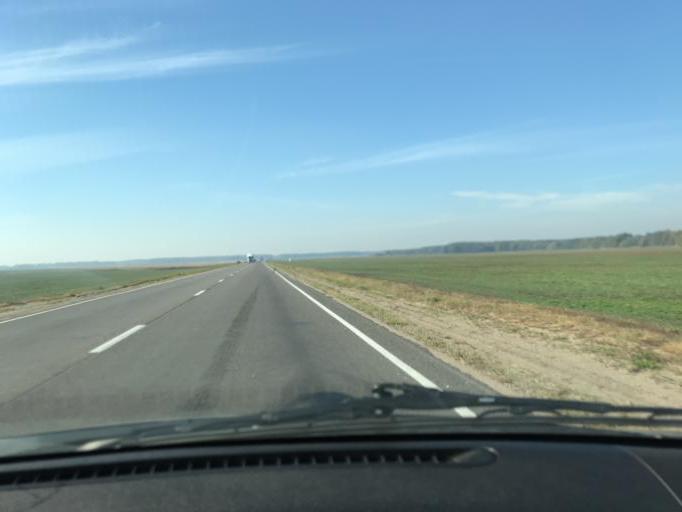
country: BY
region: Brest
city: Horad Luninyets
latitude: 52.3026
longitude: 26.4789
